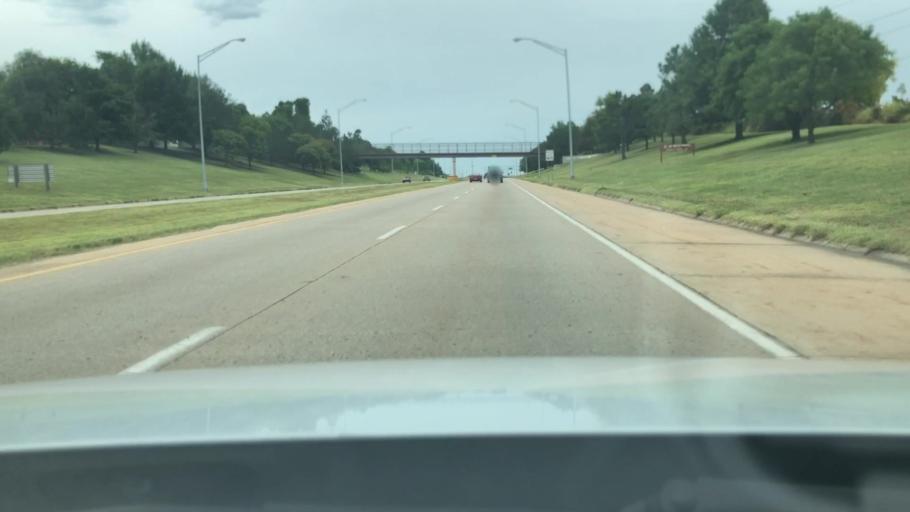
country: US
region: Oklahoma
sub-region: Tulsa County
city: Tulsa
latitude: 36.1709
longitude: -96.0008
